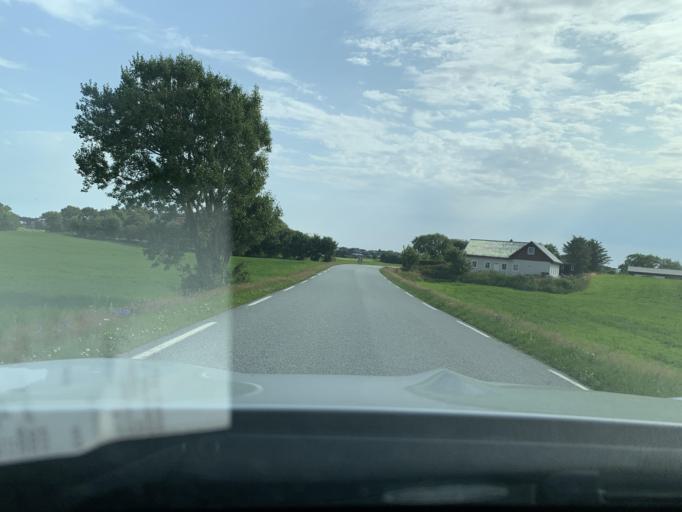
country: NO
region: Rogaland
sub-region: Time
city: Bryne
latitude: 58.7288
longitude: 5.5865
